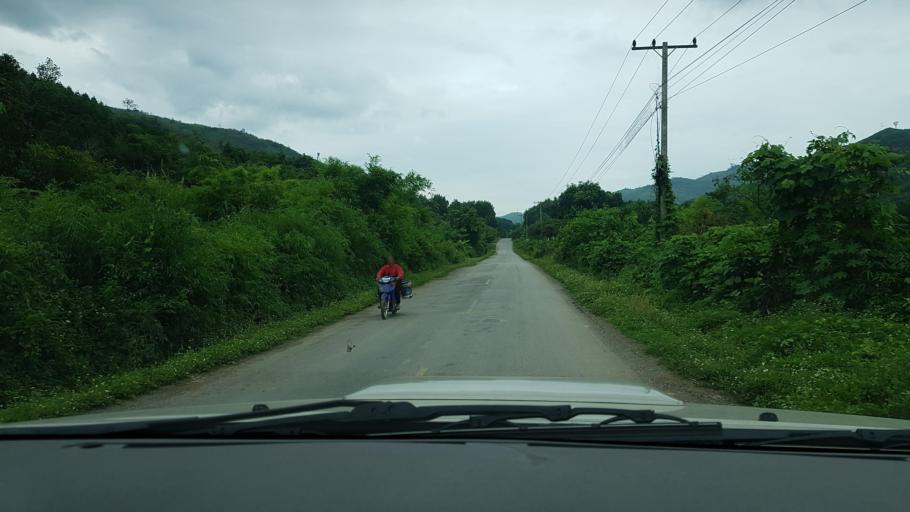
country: LA
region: Loungnamtha
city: Muang Nale
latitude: 20.2260
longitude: 101.5560
